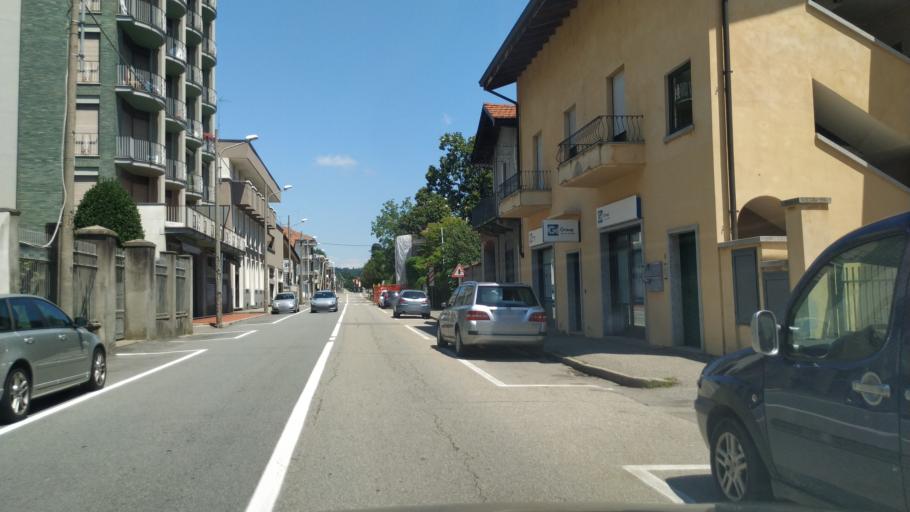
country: IT
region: Piedmont
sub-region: Provincia di Novara
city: Borgomanero
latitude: 45.7005
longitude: 8.4659
